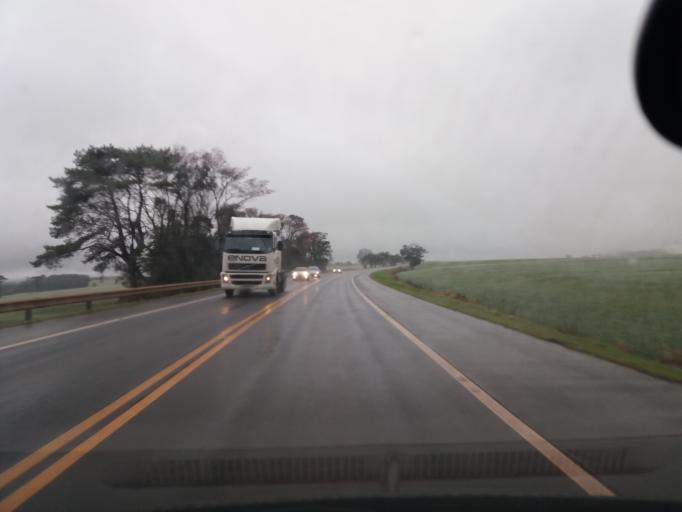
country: BR
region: Parana
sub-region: Campo Mourao
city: Campo Mourao
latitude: -24.3062
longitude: -52.6066
